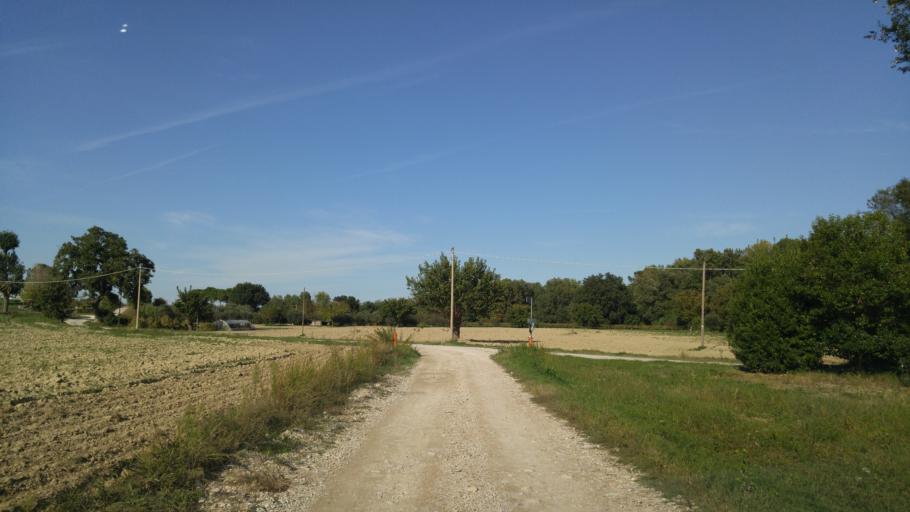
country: IT
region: The Marches
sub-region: Provincia di Pesaro e Urbino
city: Bellocchi
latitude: 43.7918
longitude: 13.0225
